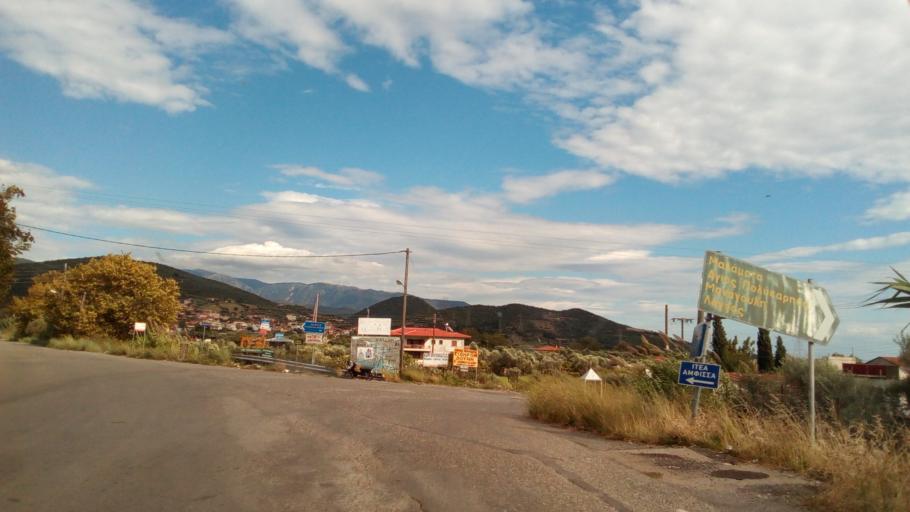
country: GR
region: West Greece
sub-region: Nomos Aitolias kai Akarnanias
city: Nafpaktos
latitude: 38.4147
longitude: 21.8821
